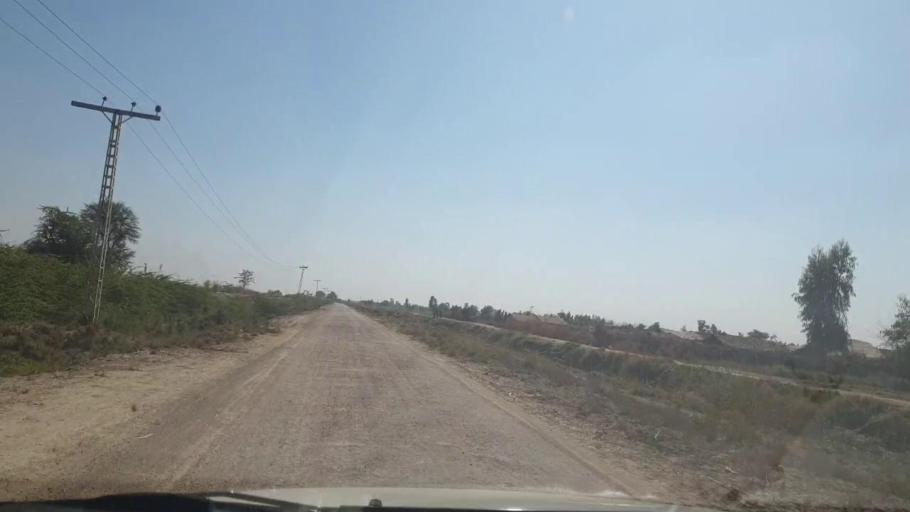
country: PK
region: Sindh
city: Mirpur Khas
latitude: 25.5026
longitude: 69.1353
